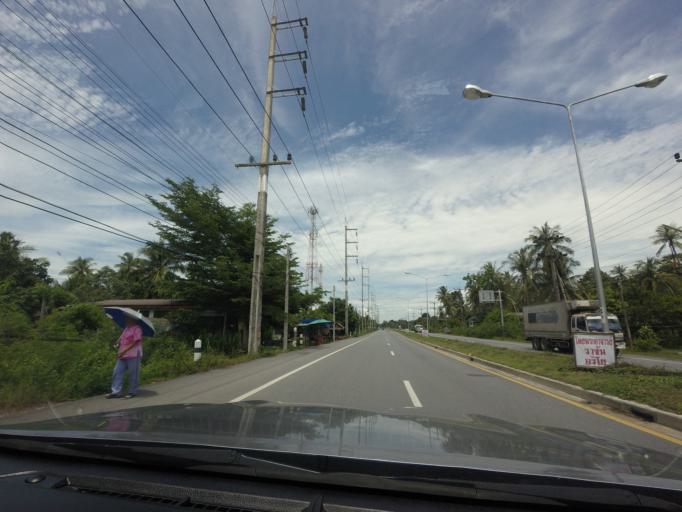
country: TH
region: Songkhla
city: Krasae Sin
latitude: 7.6091
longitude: 100.3991
